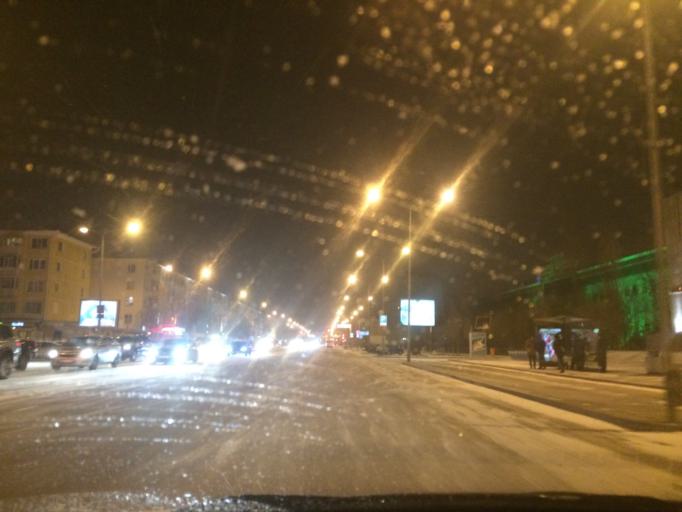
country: KZ
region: Astana Qalasy
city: Astana
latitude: 51.1856
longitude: 71.4083
